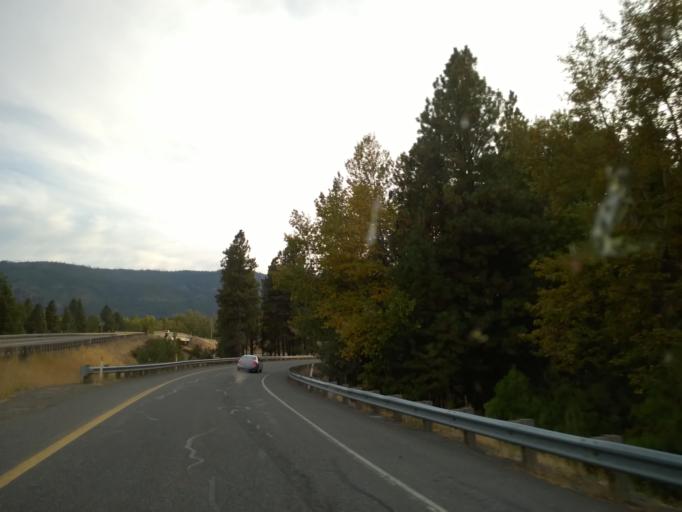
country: US
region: Washington
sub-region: Kittitas County
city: Cle Elum
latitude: 47.1846
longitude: -120.9022
